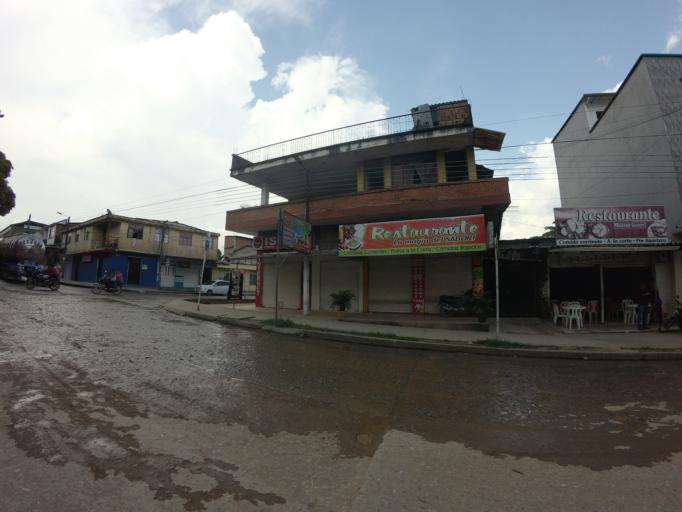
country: CO
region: Putumayo
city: Mocoa
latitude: 1.1513
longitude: -76.6483
